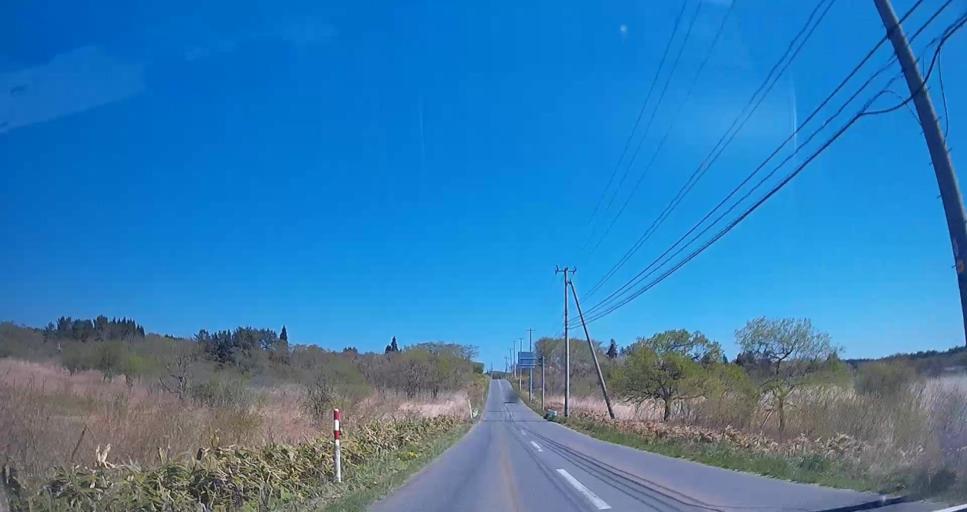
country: JP
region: Aomori
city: Misawa
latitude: 40.9147
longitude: 141.3739
